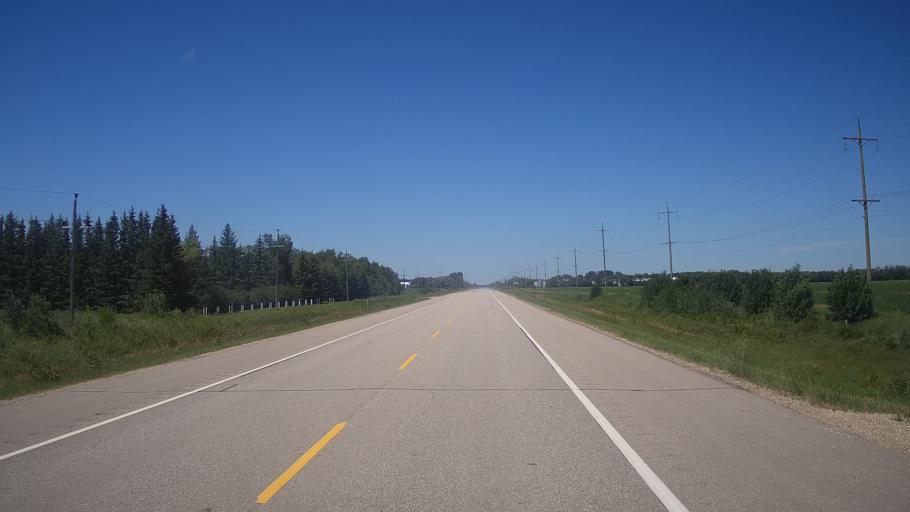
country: CA
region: Manitoba
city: Neepawa
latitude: 50.2252
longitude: -99.3053
